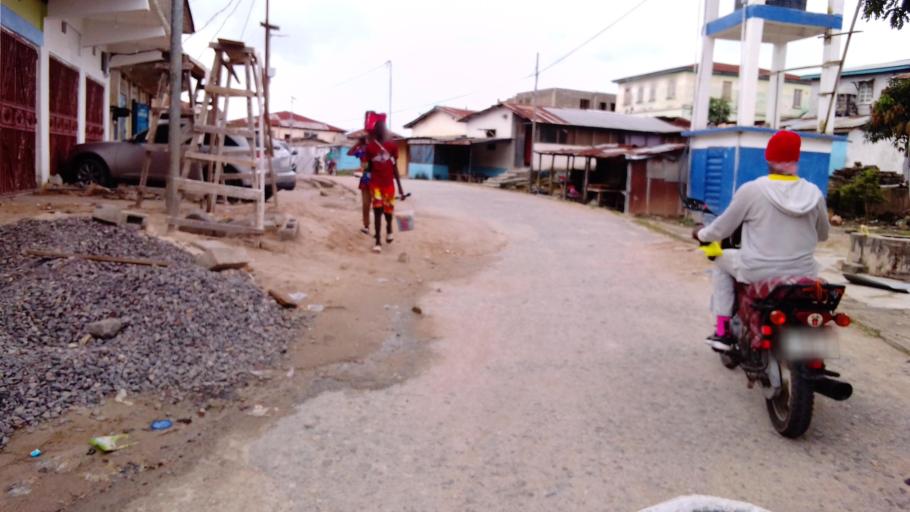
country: SL
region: Eastern Province
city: Koidu
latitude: 8.6438
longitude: -10.9759
